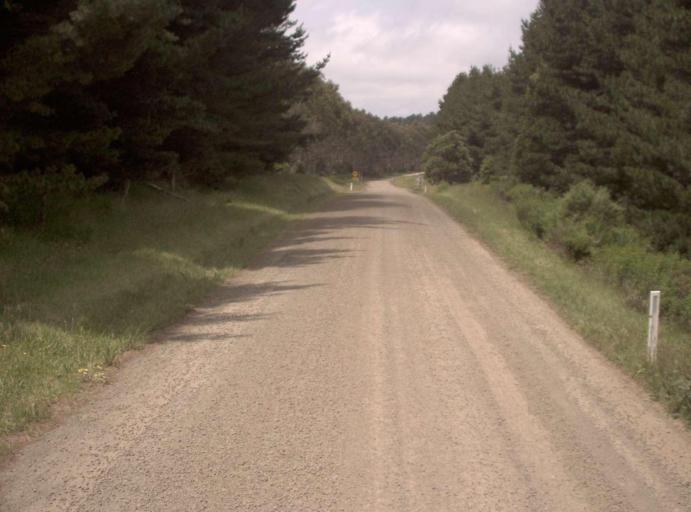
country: AU
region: Victoria
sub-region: Latrobe
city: Traralgon
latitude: -38.4057
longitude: 146.6394
